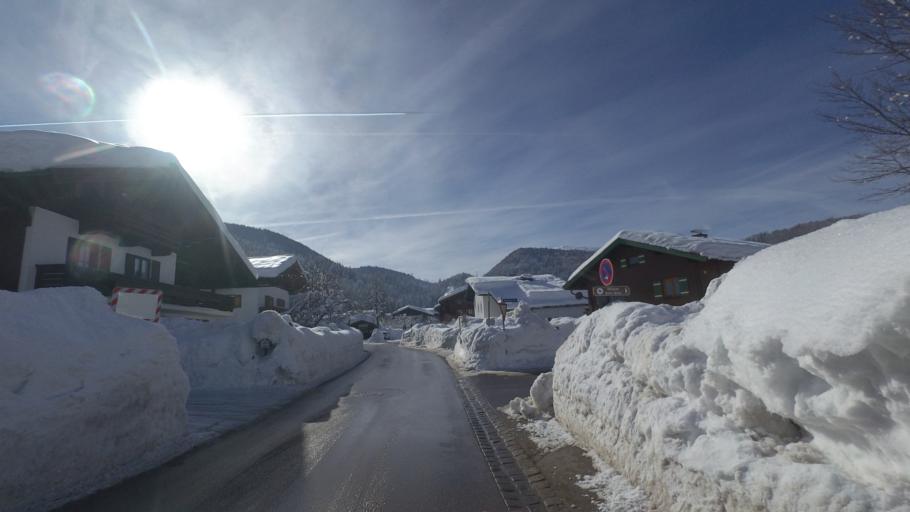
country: DE
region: Bavaria
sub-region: Upper Bavaria
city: Reit im Winkl
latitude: 47.6631
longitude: 12.4764
